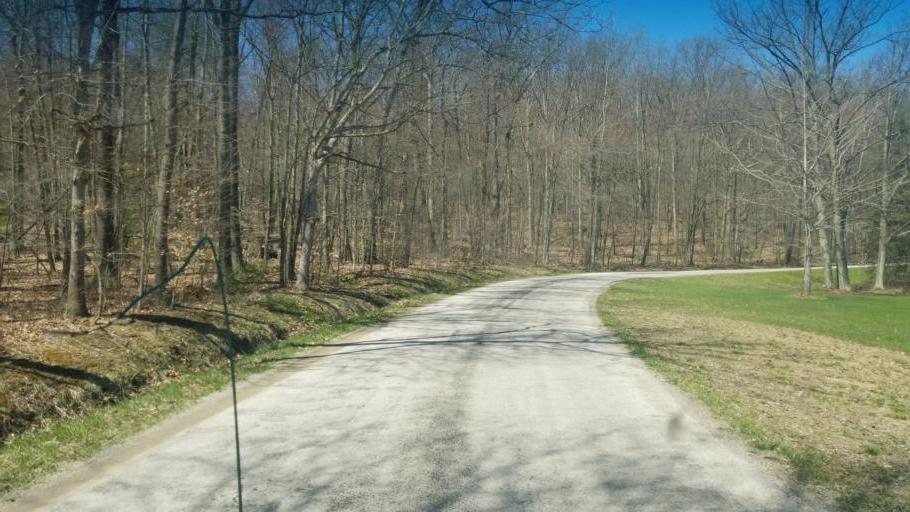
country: US
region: Ohio
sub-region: Richland County
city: Lincoln Heights
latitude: 40.8513
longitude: -82.4467
